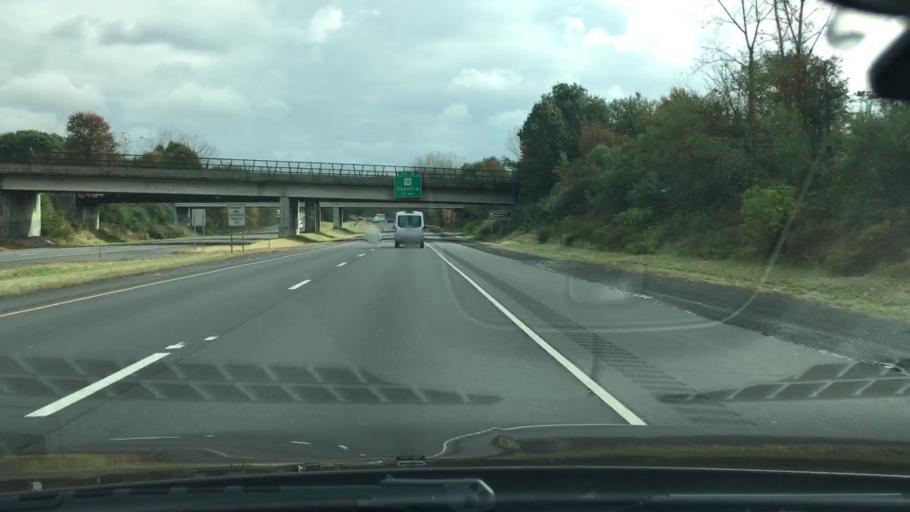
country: US
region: Connecticut
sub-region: New Haven County
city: Cheshire Village
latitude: 41.5583
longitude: -72.9043
